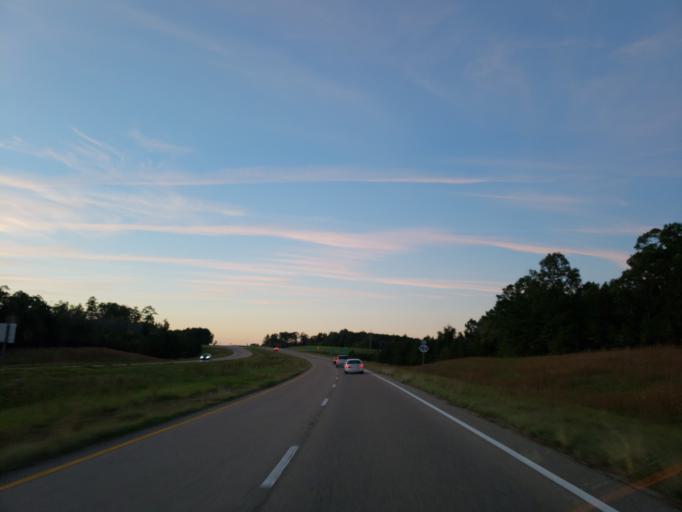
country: US
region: Mississippi
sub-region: Wayne County
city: Waynesboro
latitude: 31.6971
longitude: -88.6182
